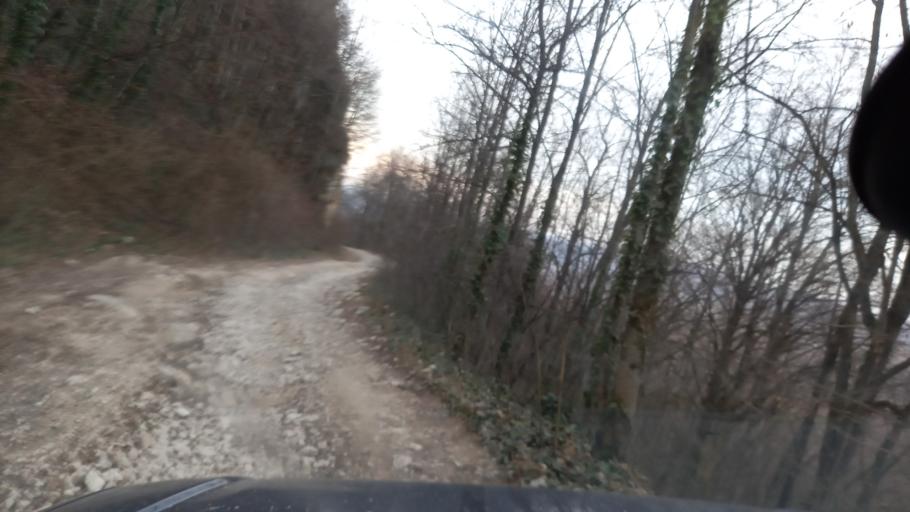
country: RU
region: Krasnodarskiy
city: Neftegorsk
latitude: 44.2199
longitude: 39.8982
